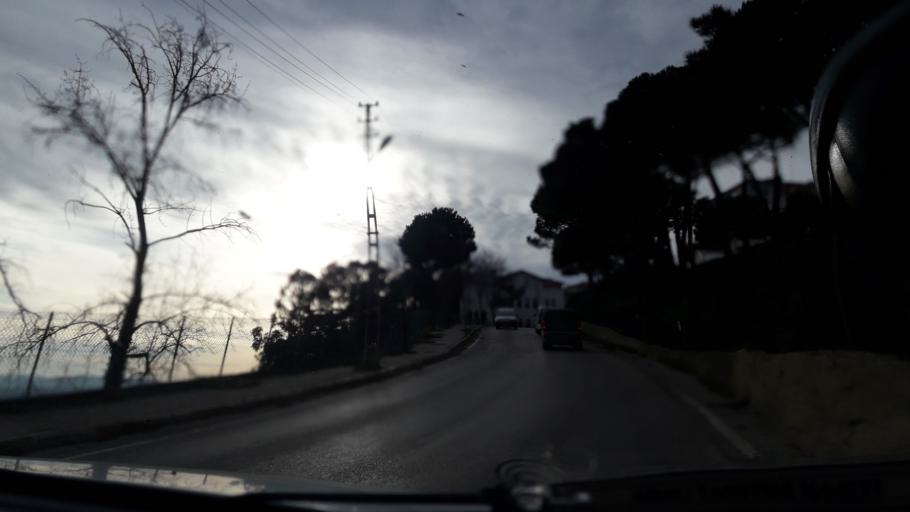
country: TR
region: Sinop
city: Sinop
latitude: 42.0237
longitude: 35.1405
